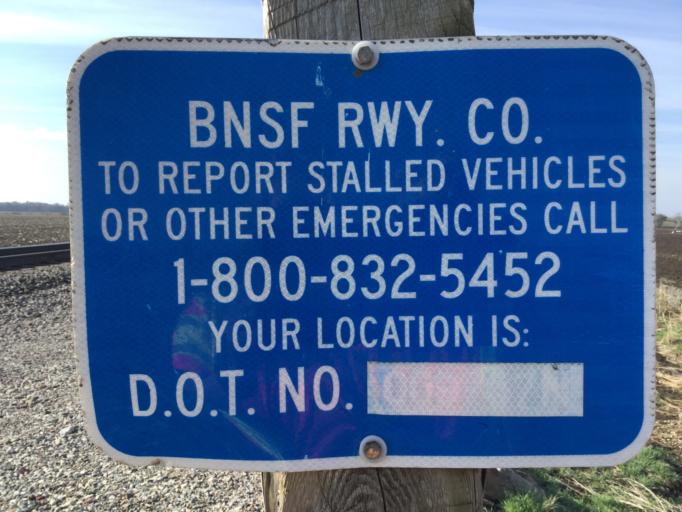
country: US
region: Kansas
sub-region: Butler County
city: Douglass
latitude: 37.5595
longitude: -97.0005
